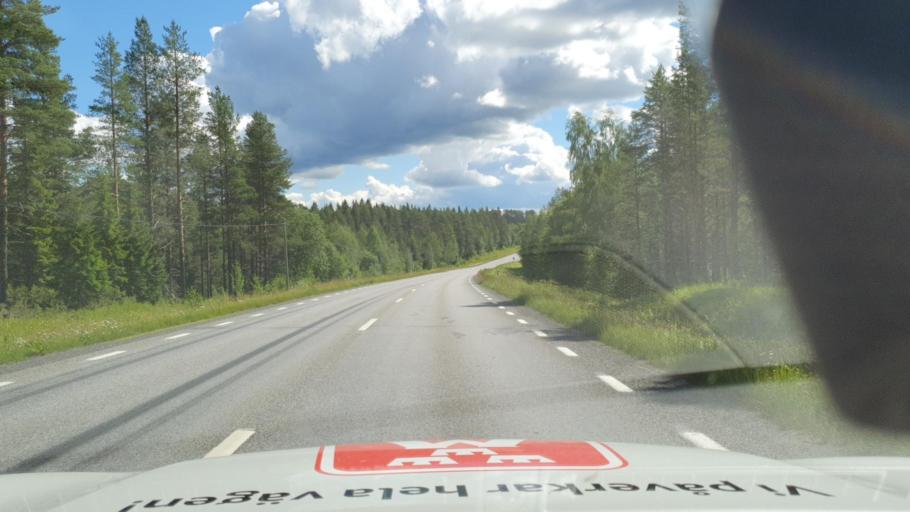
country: SE
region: Jaemtland
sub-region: OEstersunds Kommun
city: Lit
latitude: 63.3920
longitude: 14.9229
